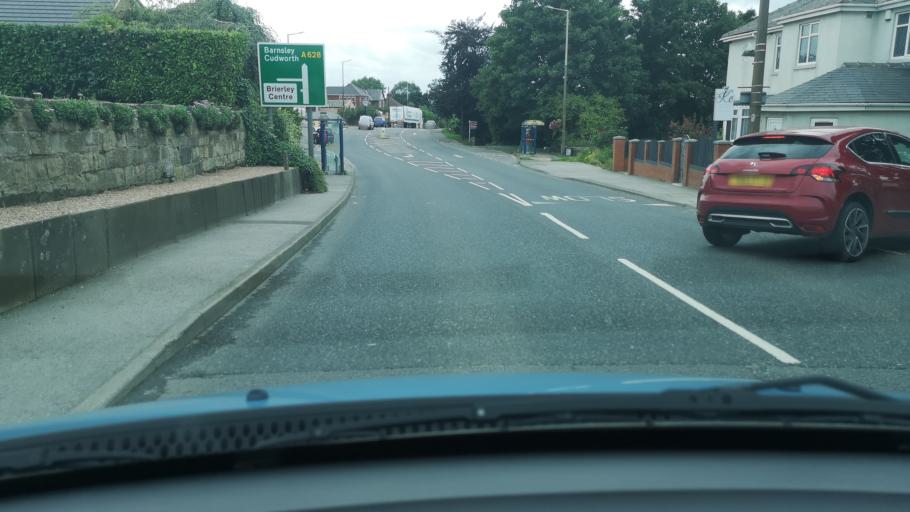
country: GB
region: England
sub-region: Barnsley
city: Grimethorpe
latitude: 53.5971
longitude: -1.3849
